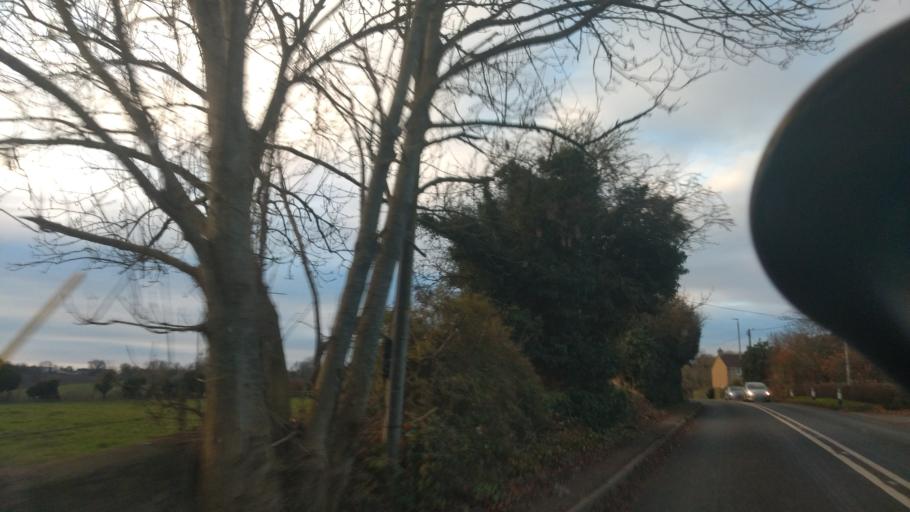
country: GB
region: England
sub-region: Somerset
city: Frome
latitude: 51.2503
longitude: -2.3068
